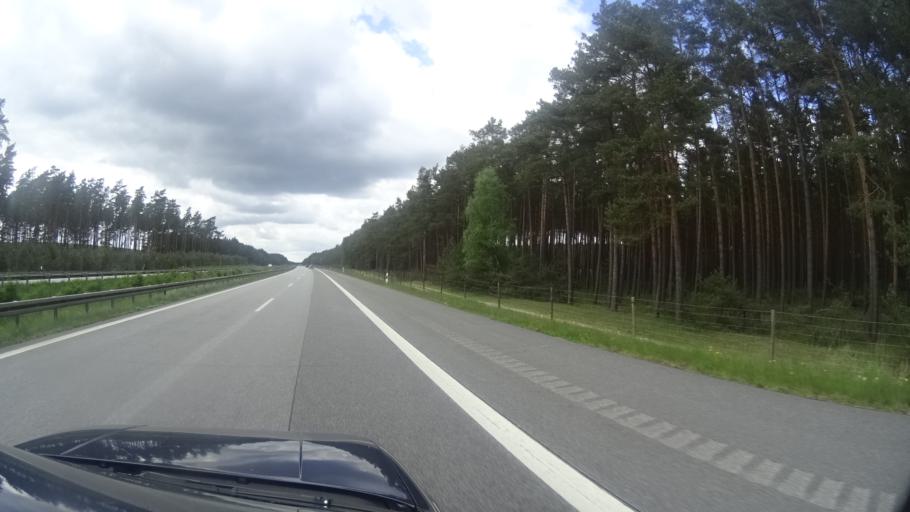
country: DE
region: Mecklenburg-Vorpommern
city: Malchow
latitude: 53.5383
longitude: 12.3446
